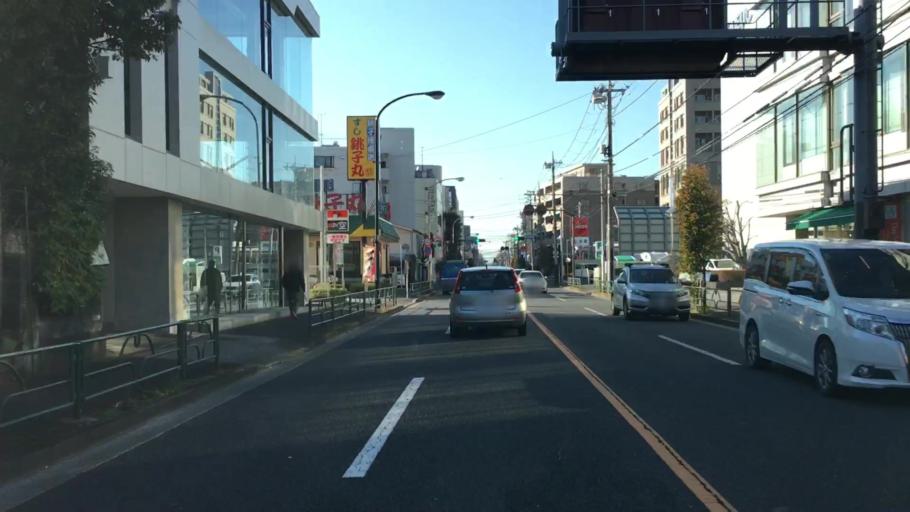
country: JP
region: Tokyo
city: Mitaka-shi
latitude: 35.6900
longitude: 139.6126
